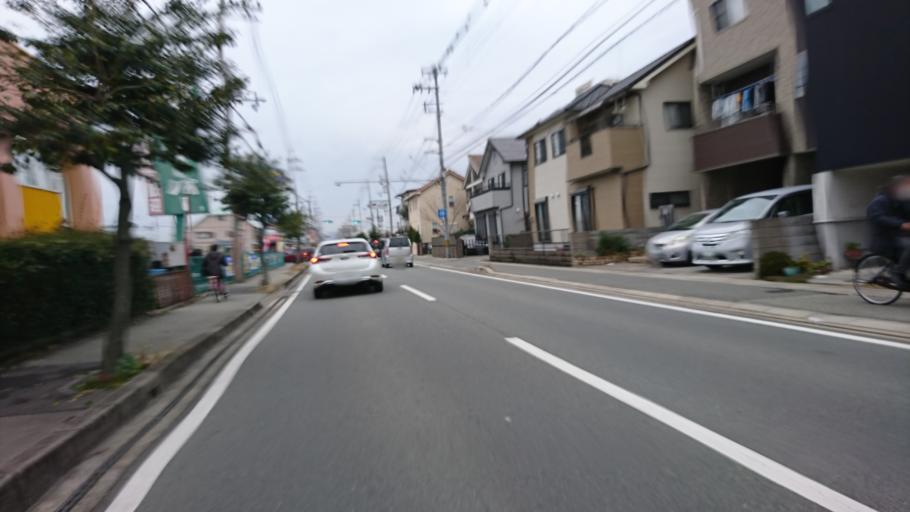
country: JP
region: Hyogo
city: Kakogawacho-honmachi
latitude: 34.7630
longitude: 134.8307
